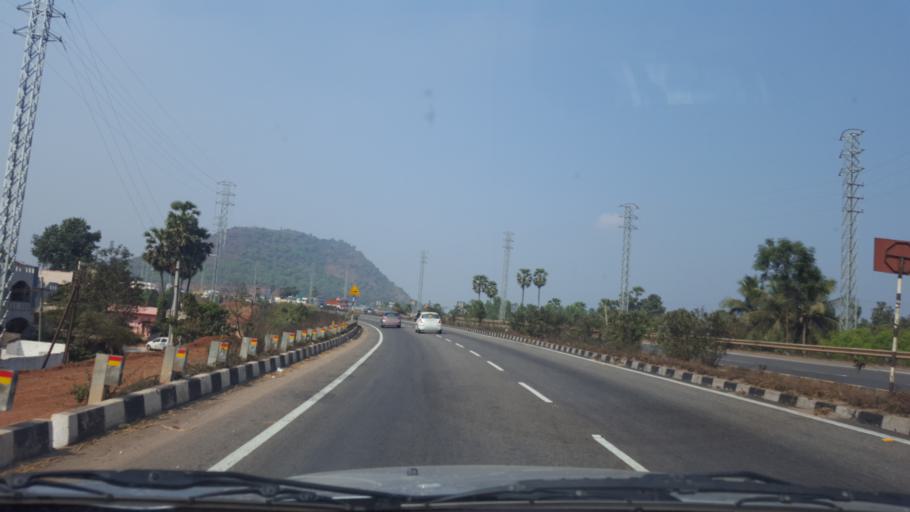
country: IN
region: Andhra Pradesh
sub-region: Vishakhapatnam
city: Bhimunipatnam
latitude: 17.8989
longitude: 83.3827
